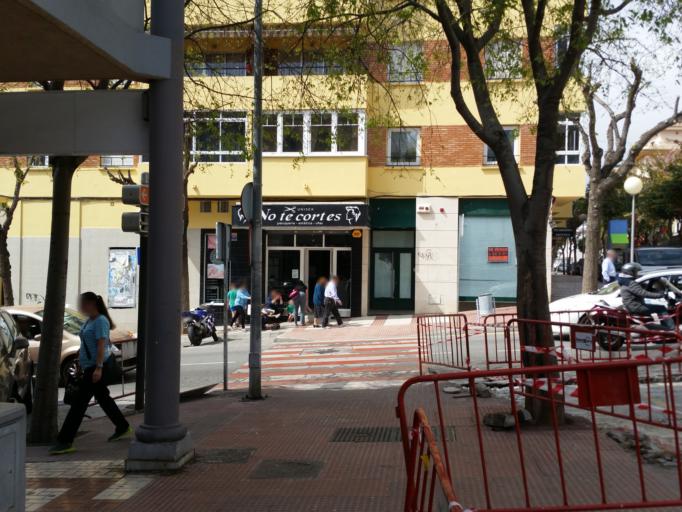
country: ES
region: Andalusia
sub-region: Provincia de Malaga
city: Torremolinos
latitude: 36.6013
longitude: -4.5321
